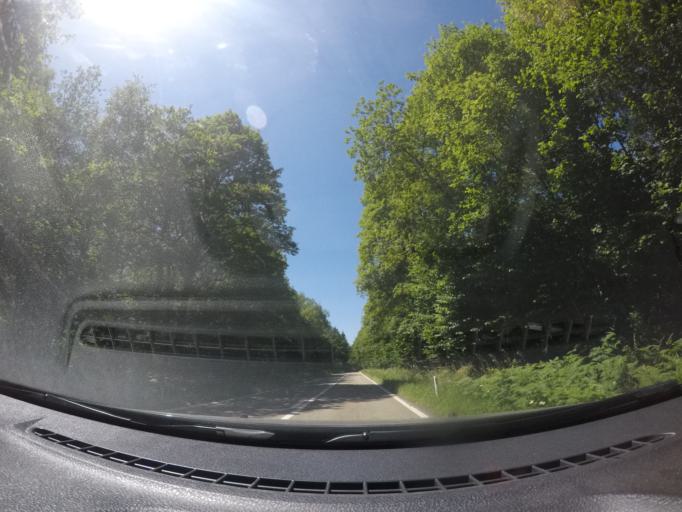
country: BE
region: Wallonia
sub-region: Province du Luxembourg
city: Daverdisse
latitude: 50.0155
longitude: 5.1757
